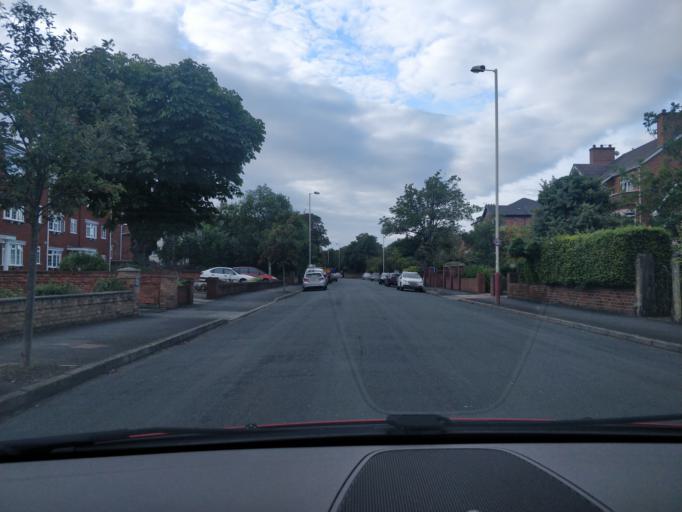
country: GB
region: England
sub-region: Sefton
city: Southport
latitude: 53.6532
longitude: -2.9873
